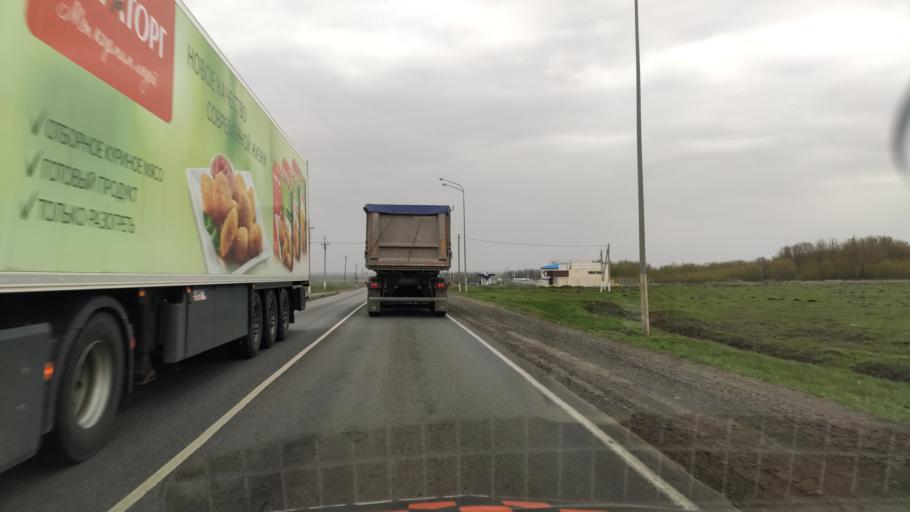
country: RU
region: Kursk
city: Gorshechnoye
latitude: 51.5316
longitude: 38.0228
